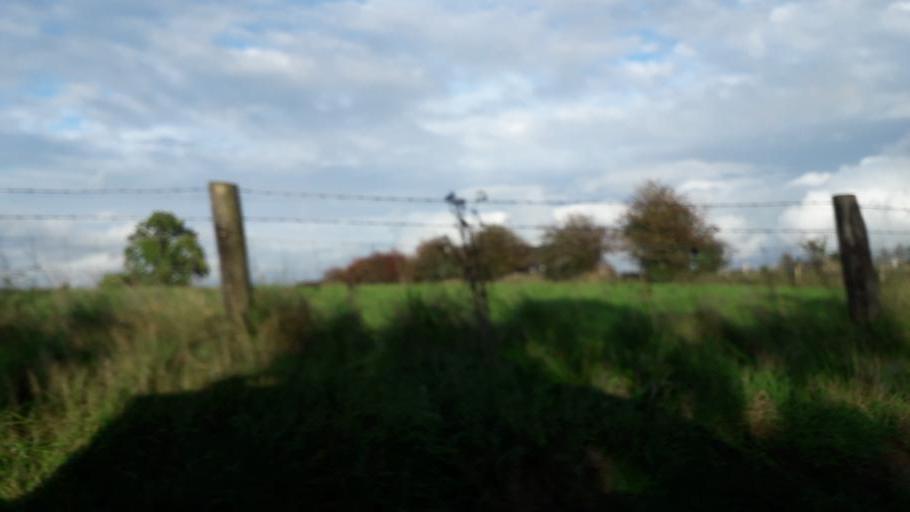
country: IE
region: Connaught
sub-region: Roscommon
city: Roscommon
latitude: 53.7832
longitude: -8.2619
